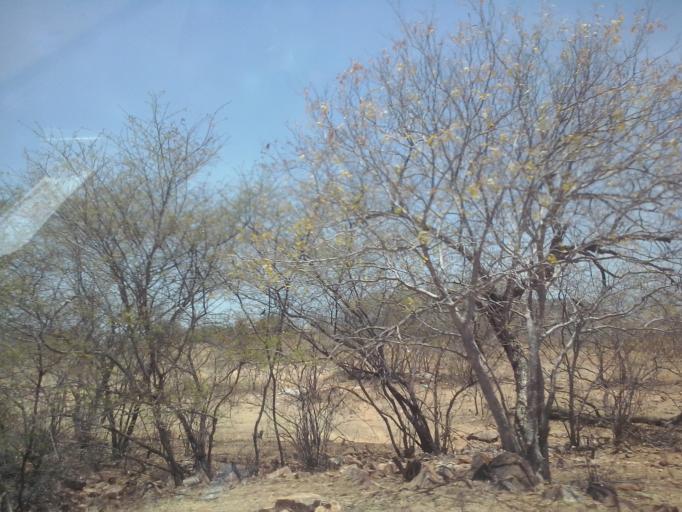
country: BR
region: Paraiba
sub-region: Paulista
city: Paulista
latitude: -6.5968
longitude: -37.6608
